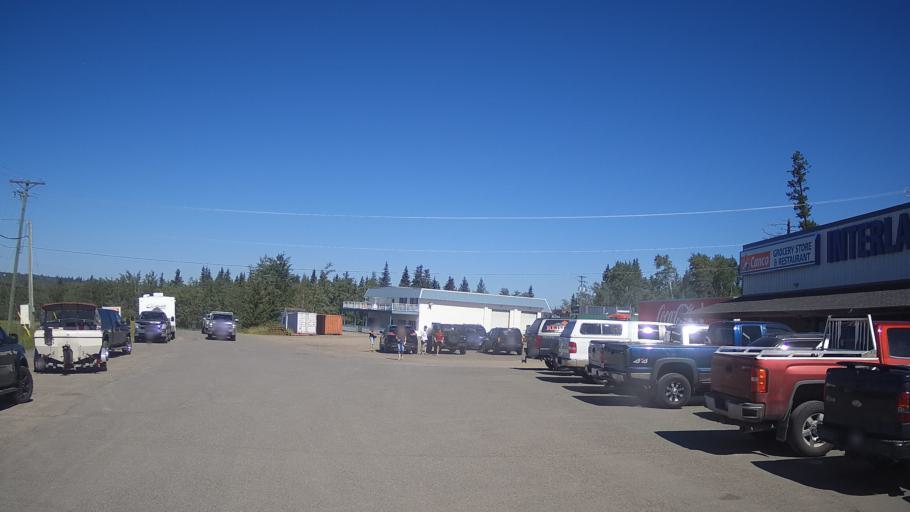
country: CA
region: British Columbia
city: Cache Creek
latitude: 51.5465
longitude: -120.9142
